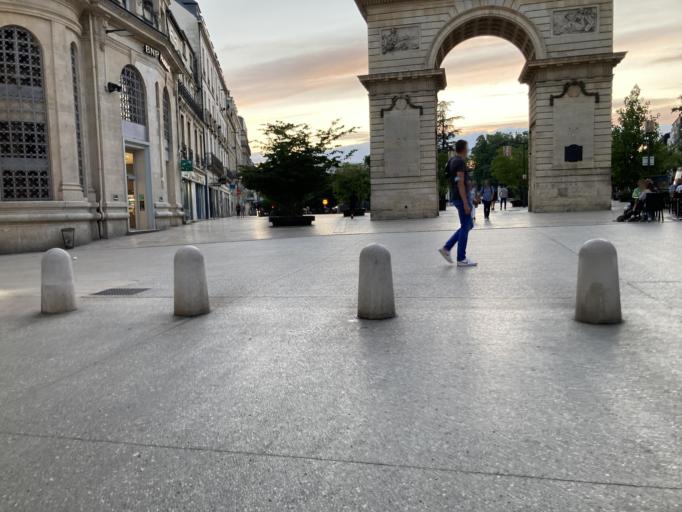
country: FR
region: Bourgogne
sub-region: Departement de la Cote-d'Or
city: Dijon
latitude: 47.3232
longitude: 5.0352
